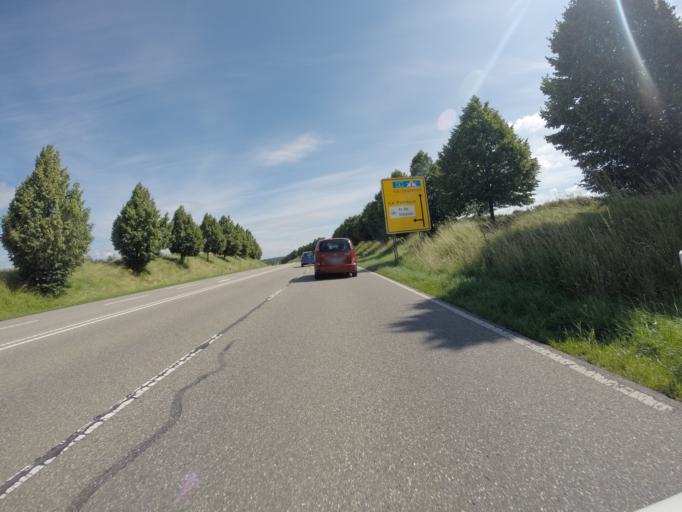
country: DE
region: Baden-Wuerttemberg
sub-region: Karlsruhe Region
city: Ettlingen
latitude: 48.9413
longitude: 8.4907
